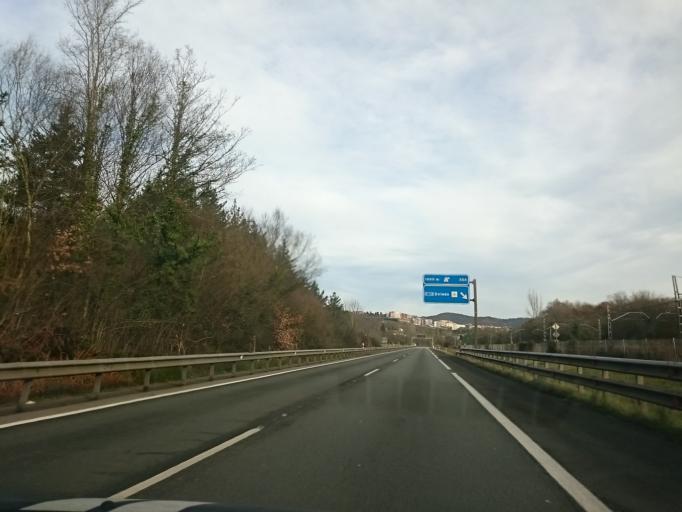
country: ES
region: Asturias
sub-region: Province of Asturias
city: Oviedo
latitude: 43.3339
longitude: -5.8700
